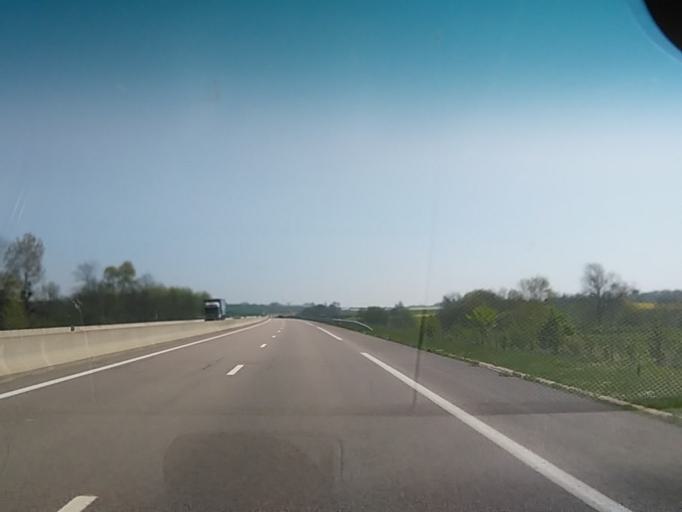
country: FR
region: Lower Normandy
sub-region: Departement de l'Orne
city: Argentan
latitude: 48.6917
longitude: -0.0102
